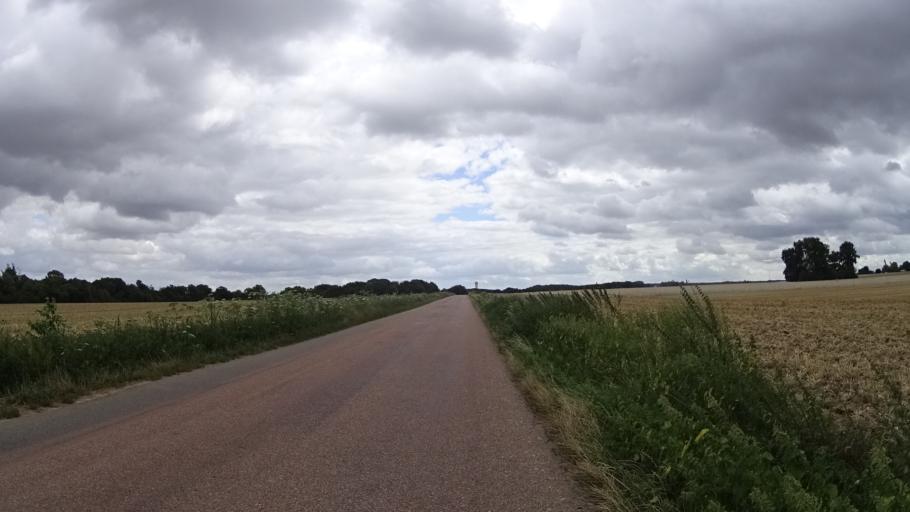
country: FR
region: Centre
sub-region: Departement du Loiret
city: Saint-Germain-des-Pres
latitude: 47.9333
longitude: 2.8715
